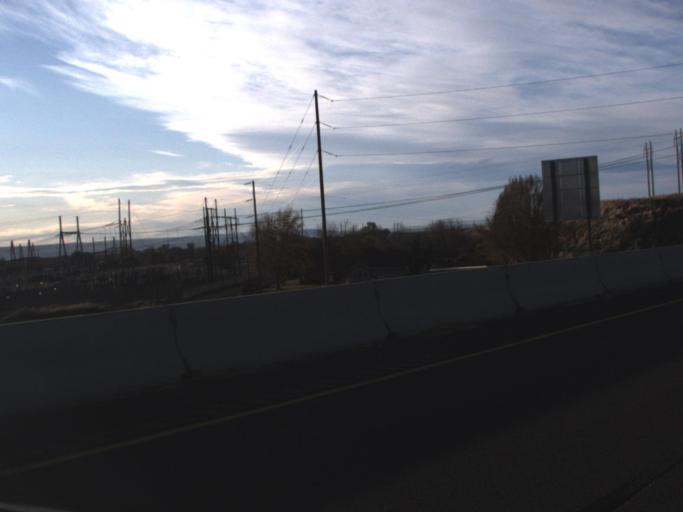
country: US
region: Washington
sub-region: Walla Walla County
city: College Place
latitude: 46.0716
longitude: -118.3759
